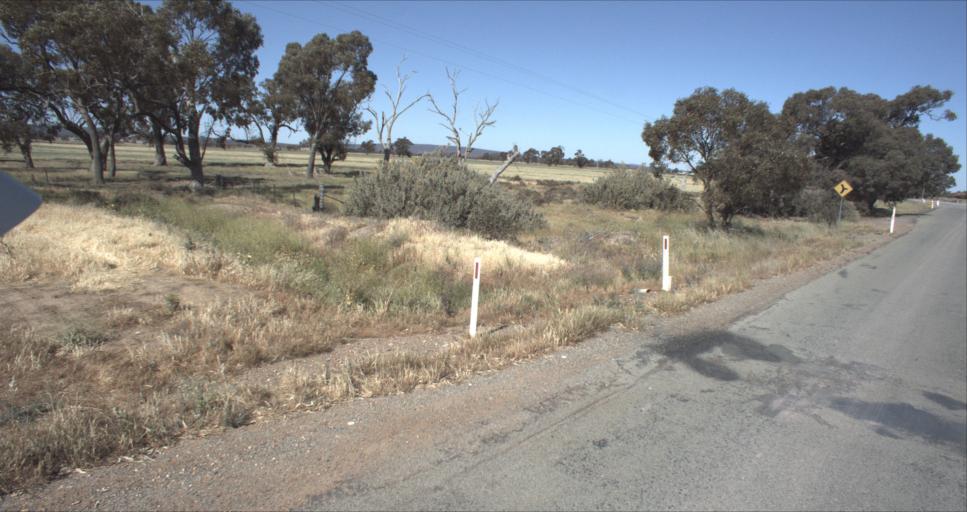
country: AU
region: New South Wales
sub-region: Leeton
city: Leeton
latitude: -34.4991
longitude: 146.3930
